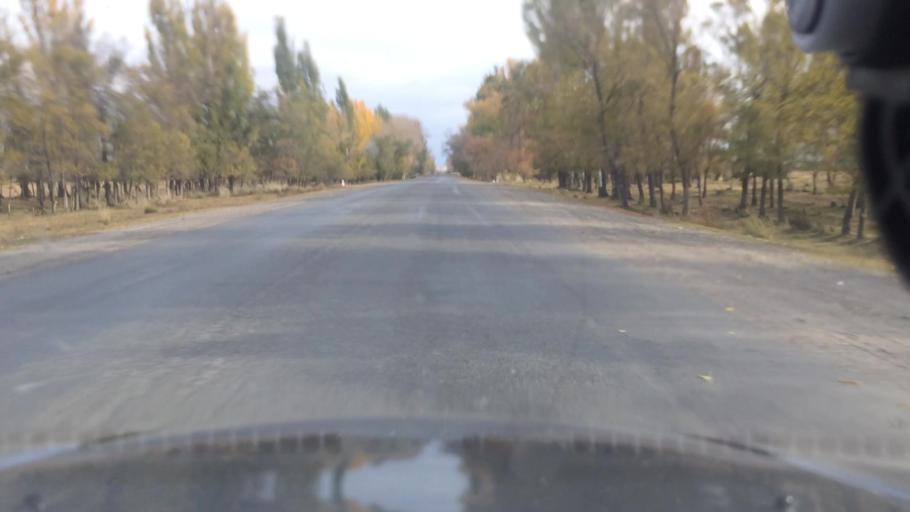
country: KG
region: Ysyk-Koel
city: Karakol
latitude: 42.5419
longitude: 78.3853
